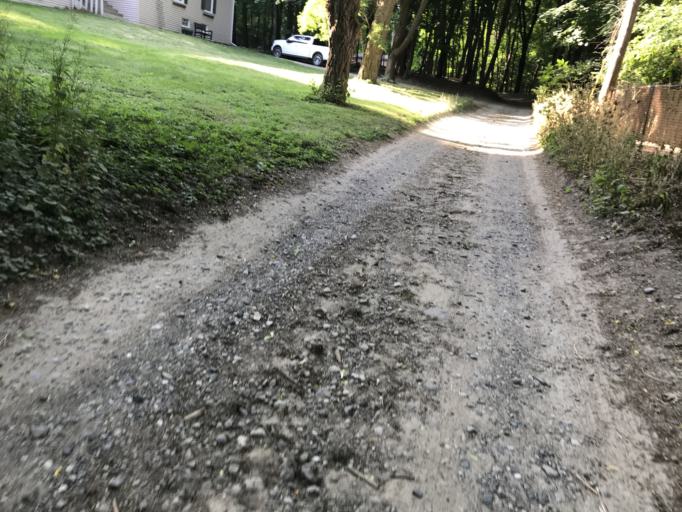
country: US
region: Michigan
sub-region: Oakland County
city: Farmington
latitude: 42.4700
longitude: -83.3840
